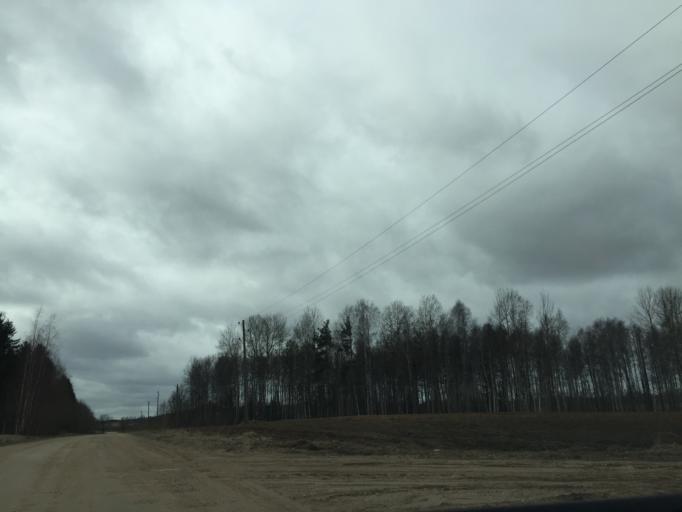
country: LV
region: Aglona
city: Aglona
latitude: 55.9415
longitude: 26.9646
